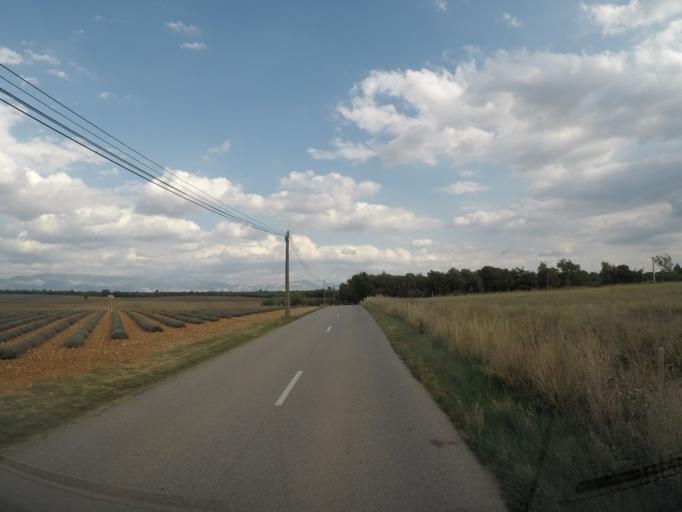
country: FR
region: Provence-Alpes-Cote d'Azur
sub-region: Departement des Alpes-de-Haute-Provence
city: Valensole
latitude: 43.8336
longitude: 6.0250
